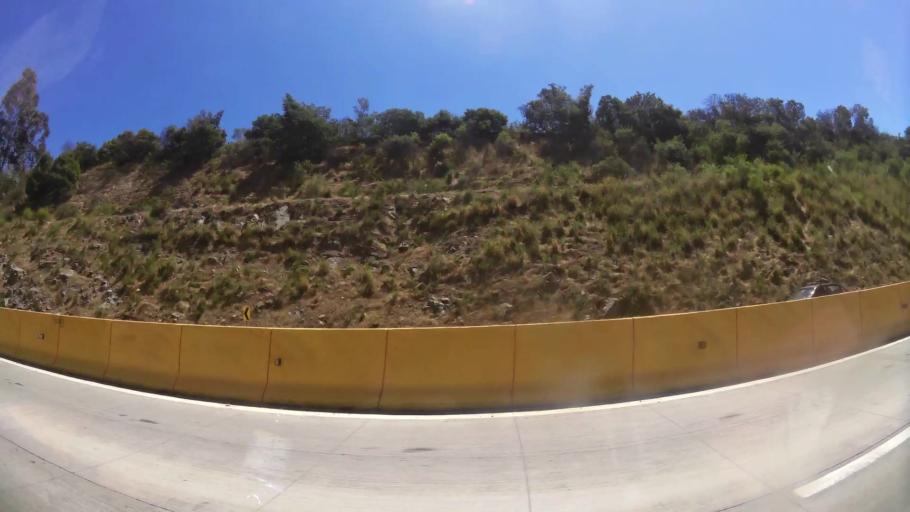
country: CL
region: Valparaiso
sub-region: Provincia de Valparaiso
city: Valparaiso
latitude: -33.0654
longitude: -71.6425
